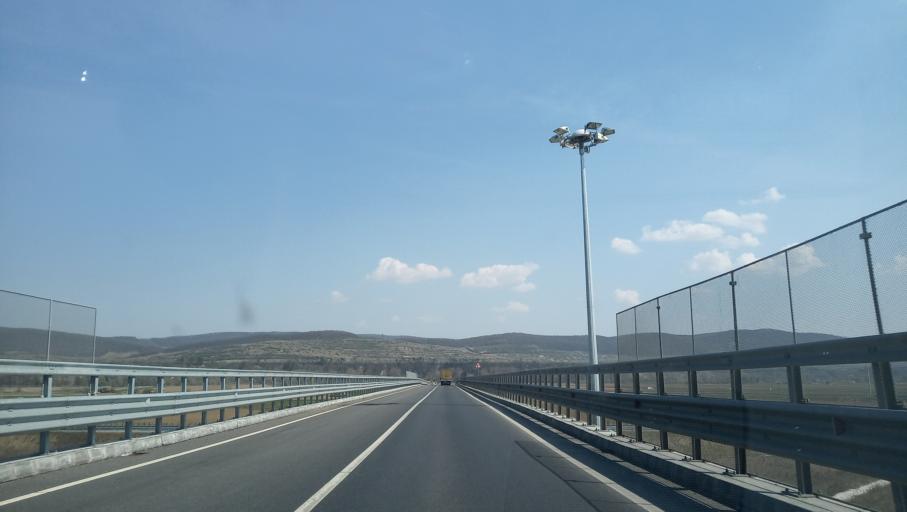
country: RO
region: Alba
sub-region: Municipiul Aiud
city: Aiud
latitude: 46.3293
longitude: 23.7273
